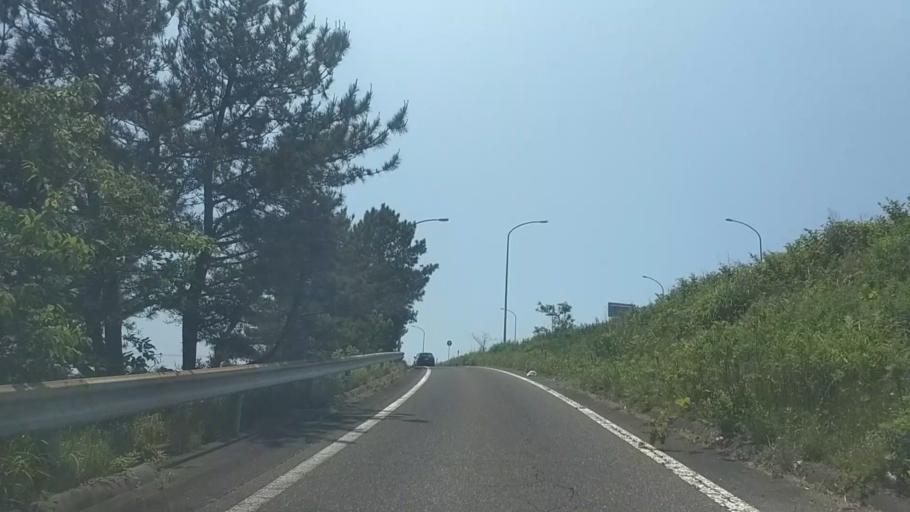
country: JP
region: Shizuoka
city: Hamamatsu
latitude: 34.6798
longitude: 137.6631
